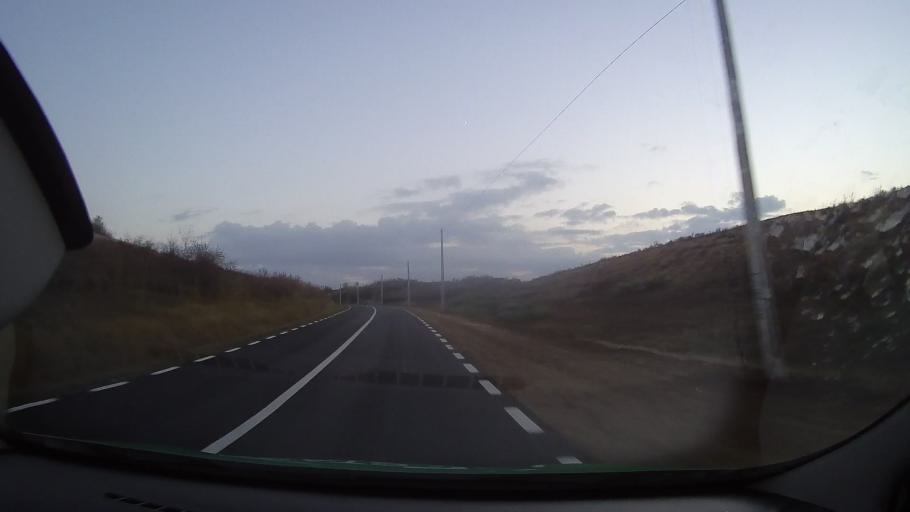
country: RO
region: Constanta
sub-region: Comuna Oltina
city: Oltina
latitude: 44.1399
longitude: 27.6653
